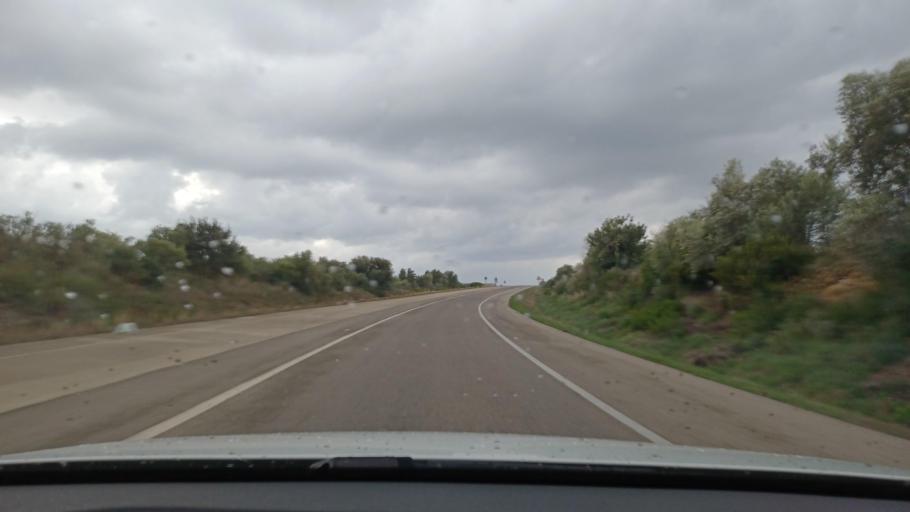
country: ES
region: Catalonia
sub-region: Provincia de Tarragona
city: Amposta
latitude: 40.7366
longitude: 0.5897
